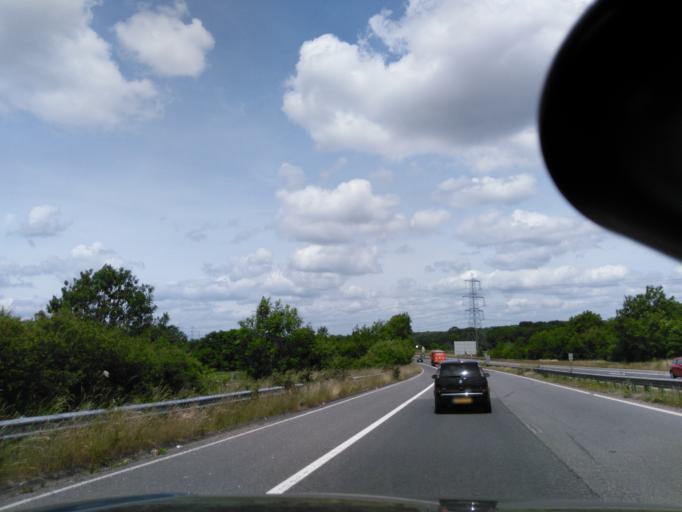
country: GB
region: England
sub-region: Hampshire
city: Totton
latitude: 50.9474
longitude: -1.5299
